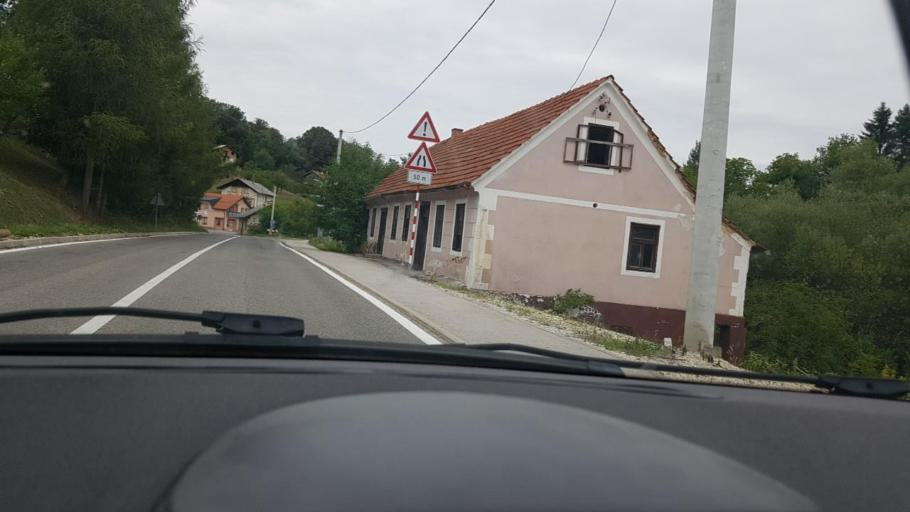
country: SI
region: Rogatec
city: Rogatec
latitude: 46.2060
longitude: 15.6914
